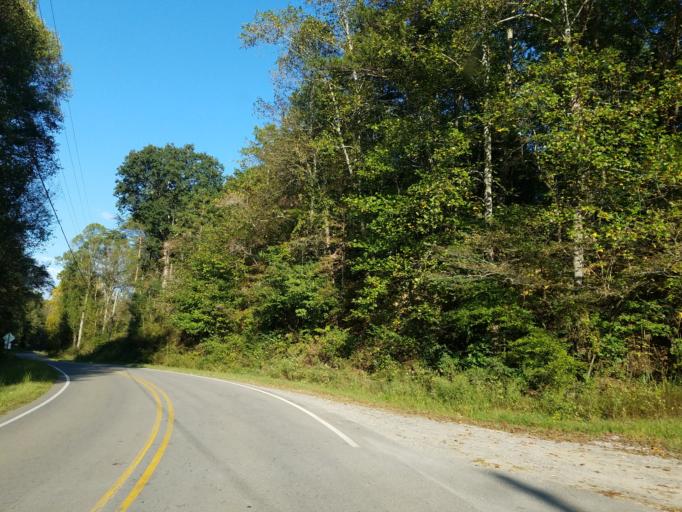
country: US
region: Georgia
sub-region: Gilmer County
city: Ellijay
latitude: 34.6427
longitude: -84.3345
